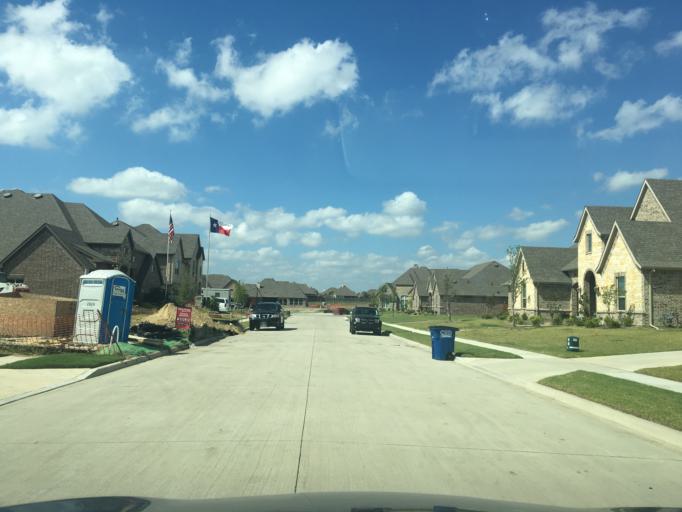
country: US
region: Texas
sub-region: Dallas County
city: Sachse
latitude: 32.9689
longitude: -96.5726
